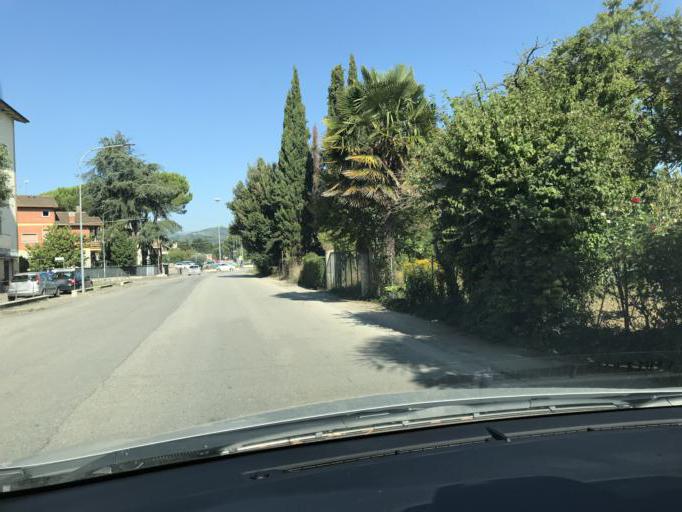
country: IT
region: Umbria
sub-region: Provincia di Perugia
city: Ponte Felcino
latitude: 43.1121
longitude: 12.4521
